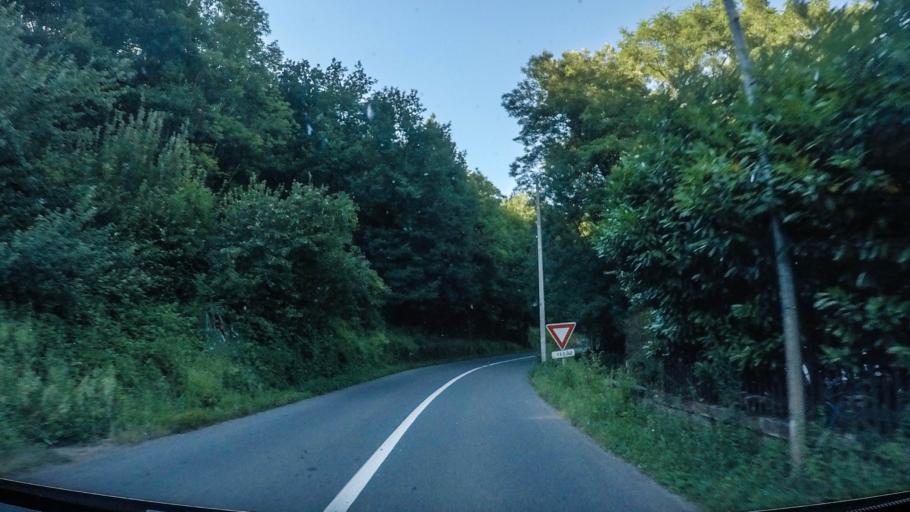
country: FR
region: Midi-Pyrenees
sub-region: Departement de l'Aveyron
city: Marcillac-Vallon
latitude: 44.4758
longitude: 2.4532
